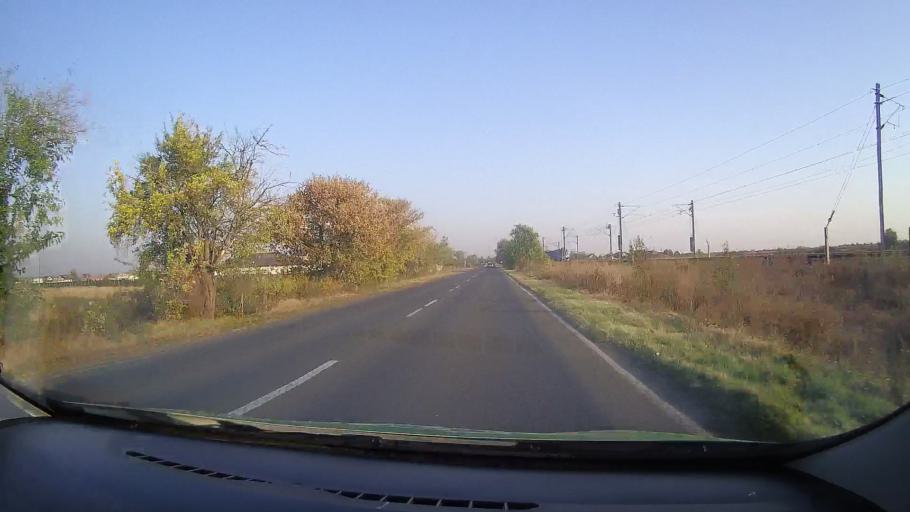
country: RO
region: Arad
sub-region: Comuna Sofronea
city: Sofronea
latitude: 46.2698
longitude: 21.3157
